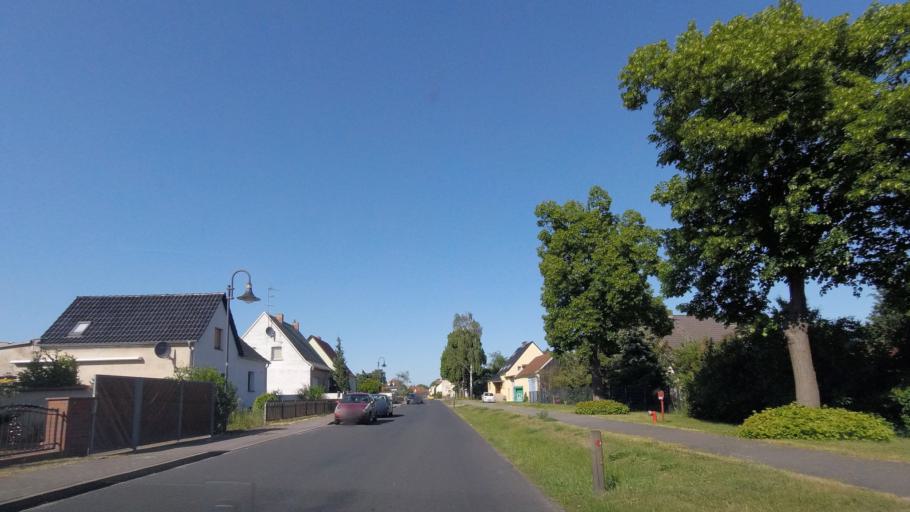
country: DE
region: Brandenburg
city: Brandenburg an der Havel
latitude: 52.3702
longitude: 12.6334
